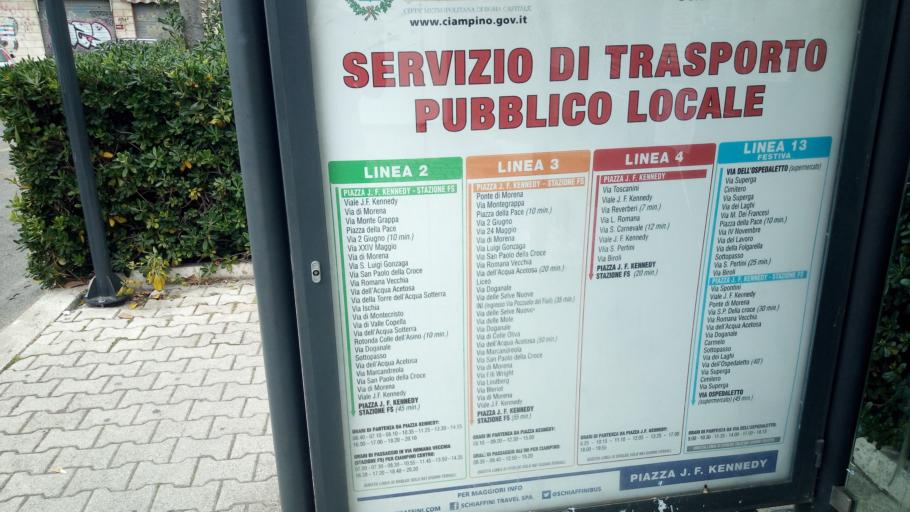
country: IT
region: Latium
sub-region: Citta metropolitana di Roma Capitale
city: Ciampino
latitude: 41.8048
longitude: 12.5999
